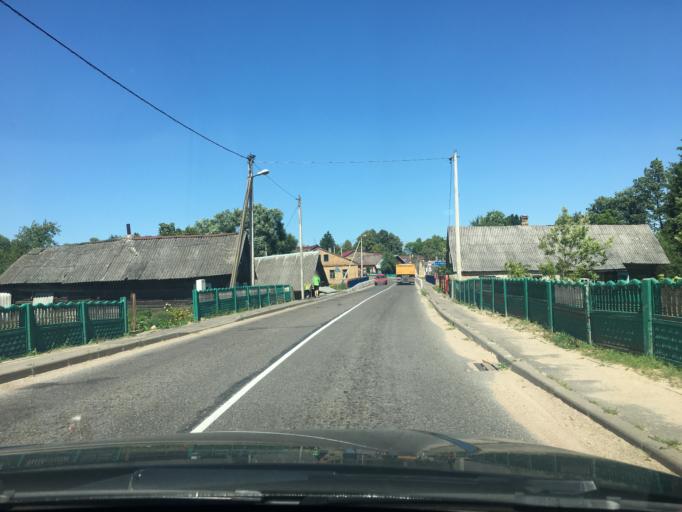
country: BY
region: Grodnenskaya
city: Hal'shany
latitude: 54.1559
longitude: 25.9073
